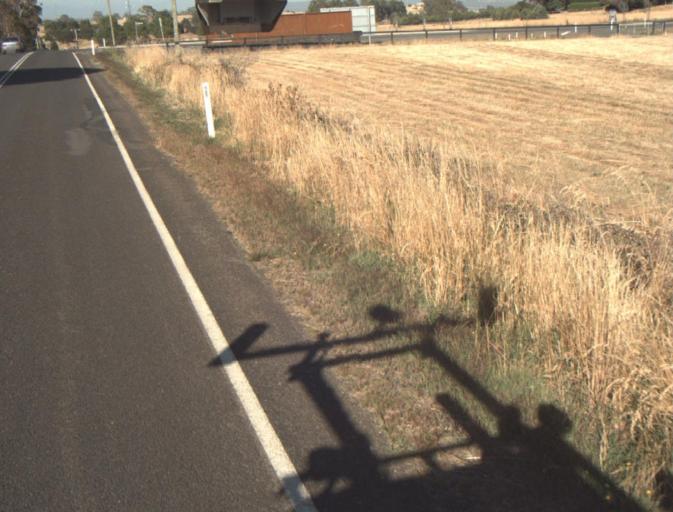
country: AU
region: Tasmania
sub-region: Launceston
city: Newstead
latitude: -41.4442
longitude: 147.2321
